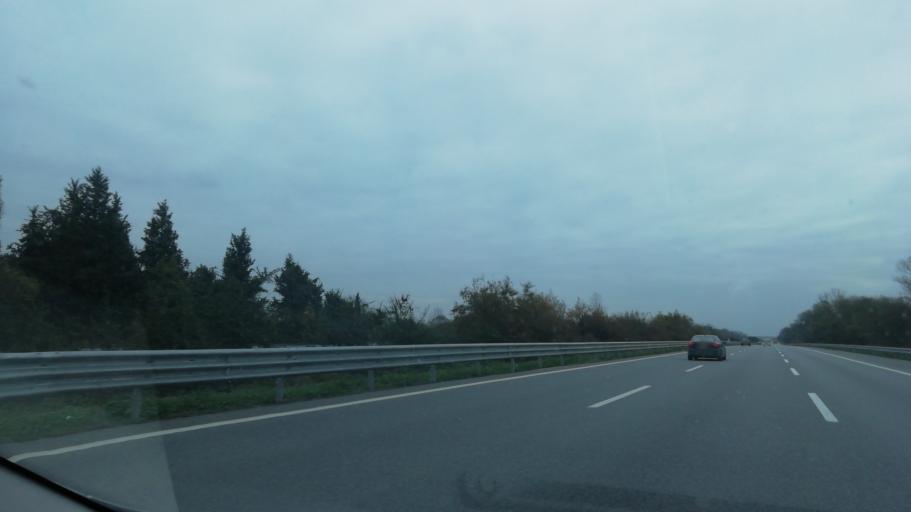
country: TR
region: Duzce
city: Cilimli
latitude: 40.8256
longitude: 31.0562
